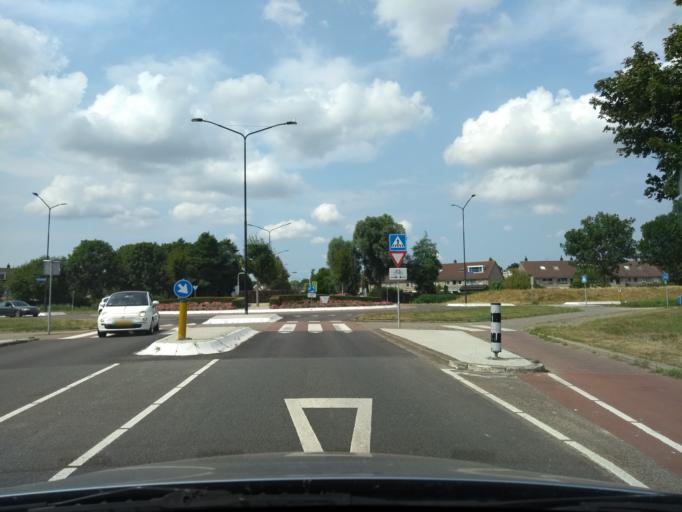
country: NL
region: North Holland
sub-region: Gemeente Heerhugowaard
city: Heerhugowaard
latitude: 52.6531
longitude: 4.8338
